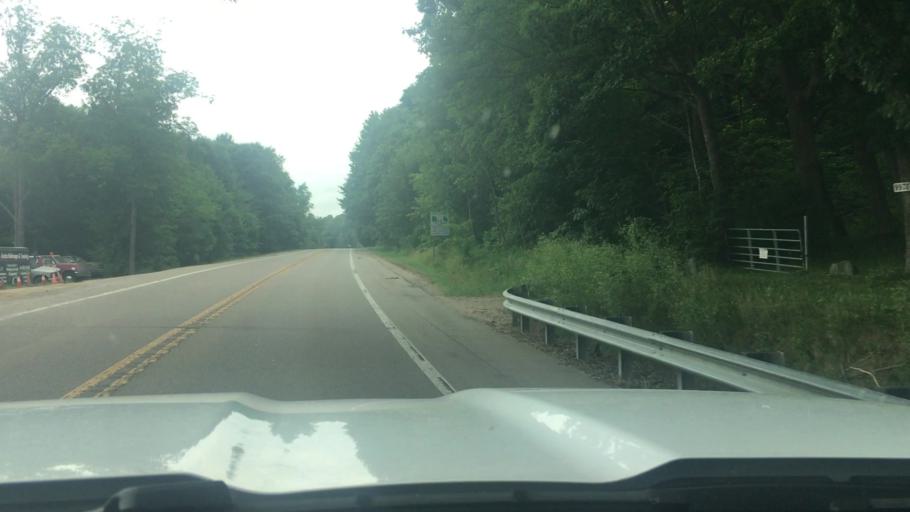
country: US
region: Michigan
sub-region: Ionia County
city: Saranac
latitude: 42.9350
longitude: -85.2717
